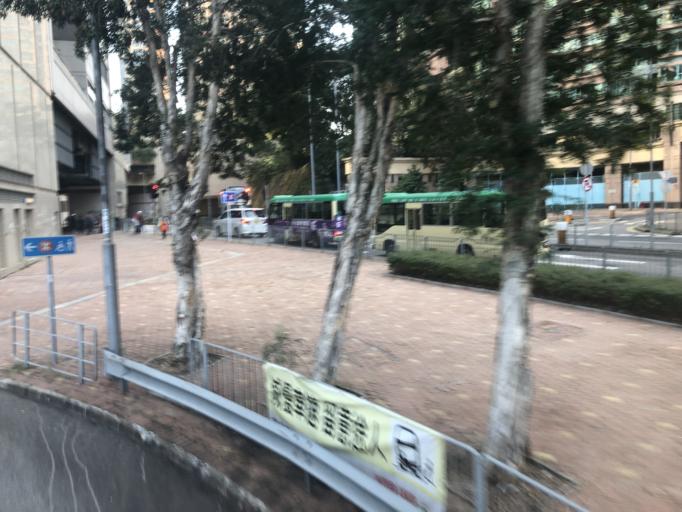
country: HK
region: Sai Kung
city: Sai Kung
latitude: 22.4278
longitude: 114.2429
